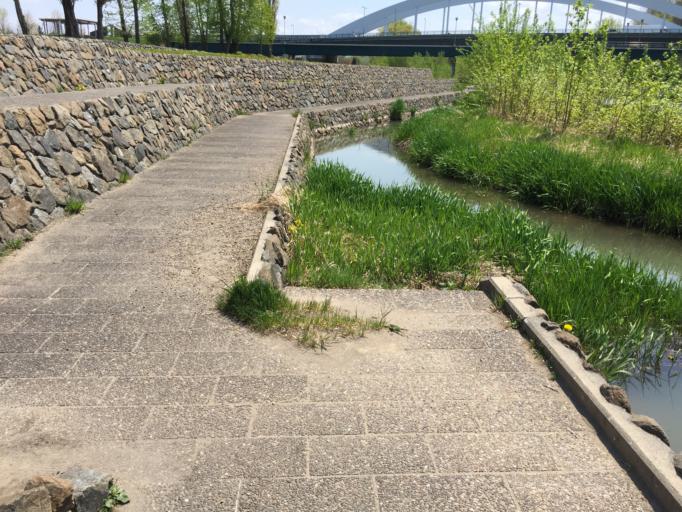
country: JP
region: Hokkaido
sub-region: Asahikawa-shi
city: Asahikawa
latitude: 43.7565
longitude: 142.3655
